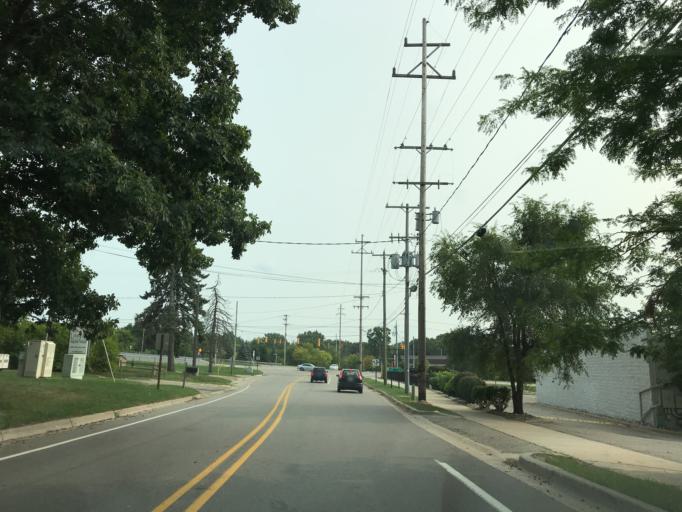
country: US
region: Michigan
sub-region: Ingham County
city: Okemos
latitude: 42.7270
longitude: -84.4475
